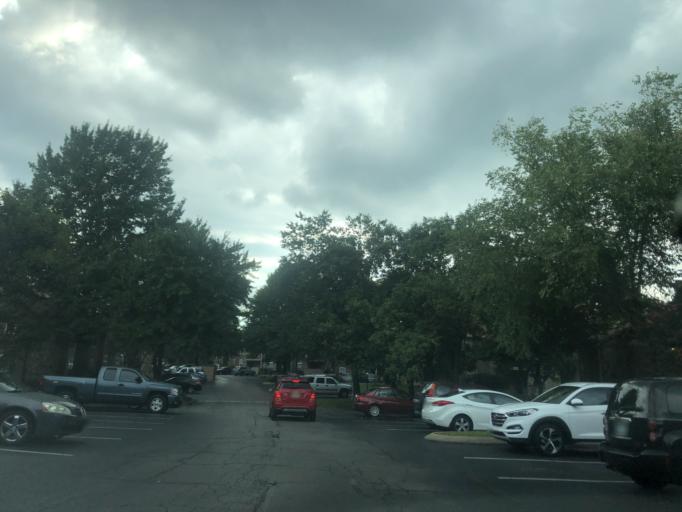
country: US
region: Tennessee
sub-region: Davidson County
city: Lakewood
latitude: 36.1692
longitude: -86.6117
